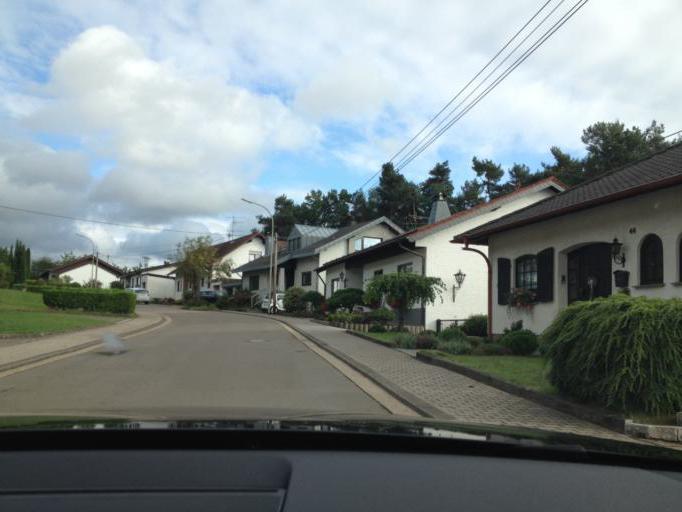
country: DE
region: Saarland
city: Namborn
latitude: 49.5163
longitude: 7.1435
